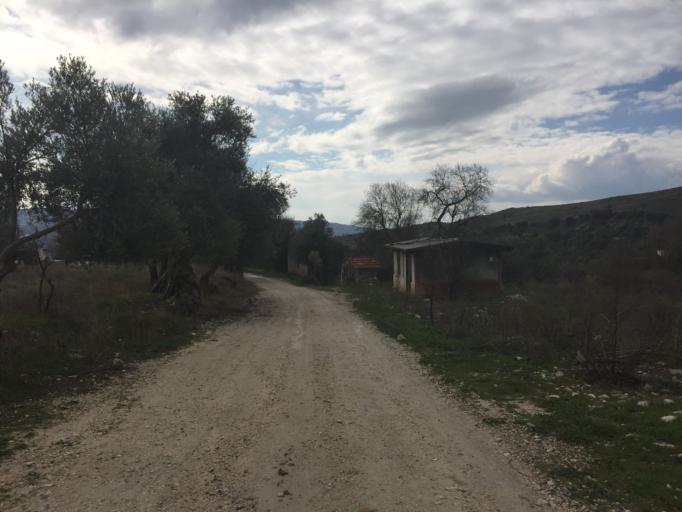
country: CY
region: Limassol
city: Pachna
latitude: 34.8913
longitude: 32.6585
